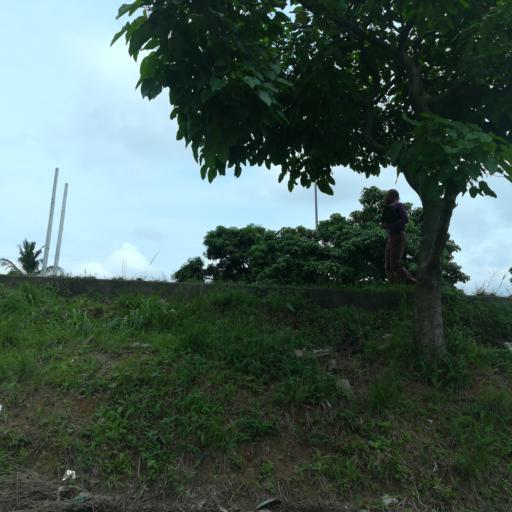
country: NG
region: Rivers
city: Port Harcourt
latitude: 4.7959
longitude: 7.0235
